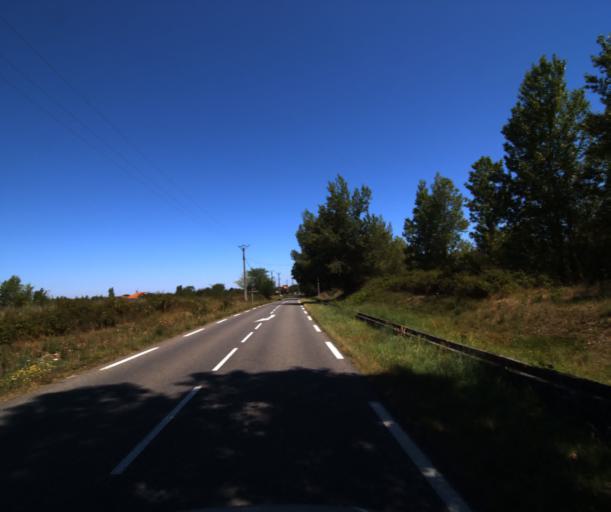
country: FR
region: Midi-Pyrenees
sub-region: Departement de la Haute-Garonne
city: Seysses
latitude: 43.4762
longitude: 1.3040
